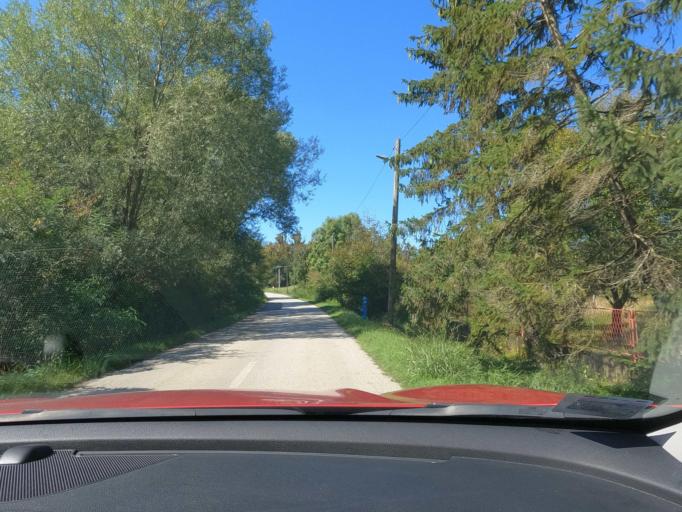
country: HR
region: Sisacko-Moslavacka
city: Petrinja
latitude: 45.4698
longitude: 16.3112
